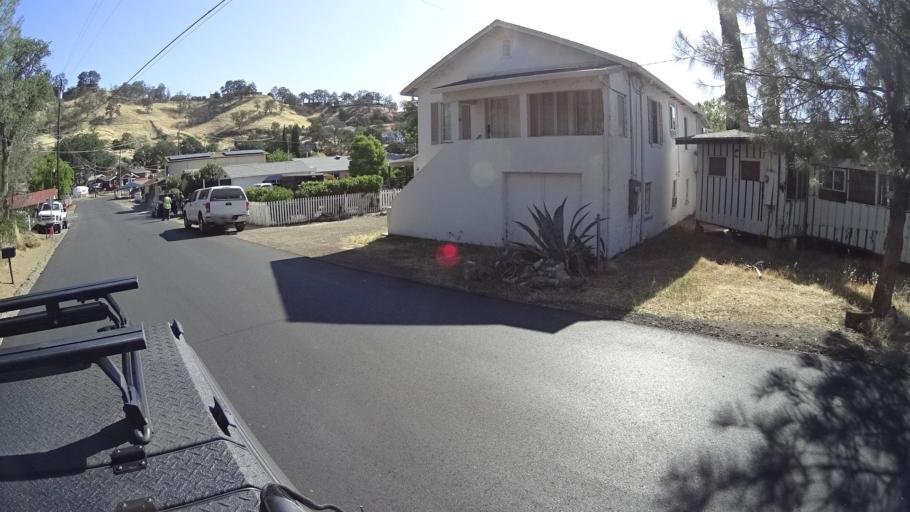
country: US
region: California
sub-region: Lake County
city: Clearlake
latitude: 38.9711
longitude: -122.6703
